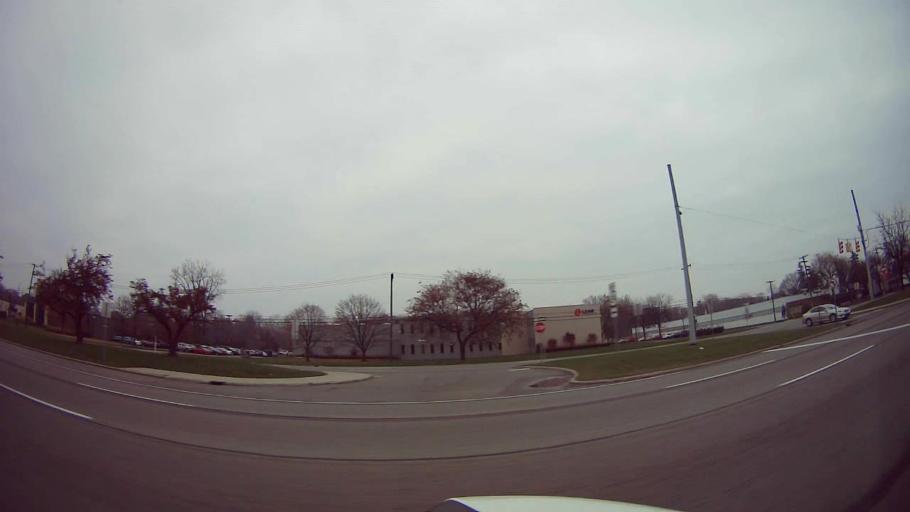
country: US
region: Michigan
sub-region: Oakland County
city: Southfield
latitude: 42.4512
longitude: -83.2785
